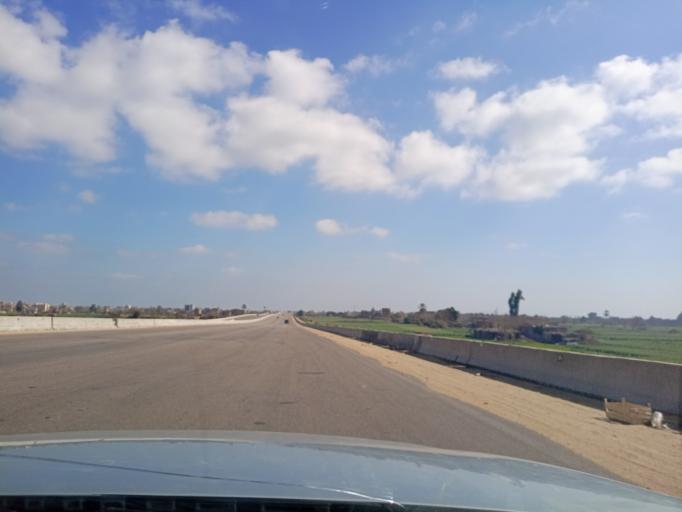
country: EG
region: Muhafazat al Minufiyah
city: Al Bajur
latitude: 30.3976
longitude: 31.0159
